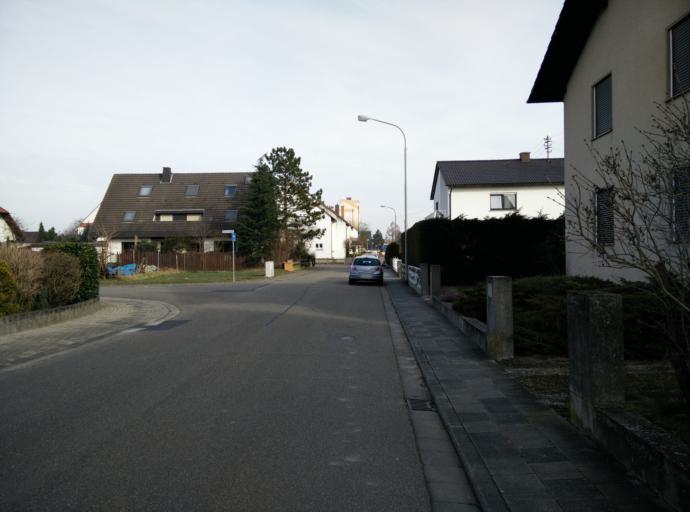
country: DE
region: Rheinland-Pfalz
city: Bohl-Iggelheim
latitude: 49.3683
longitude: 8.3054
